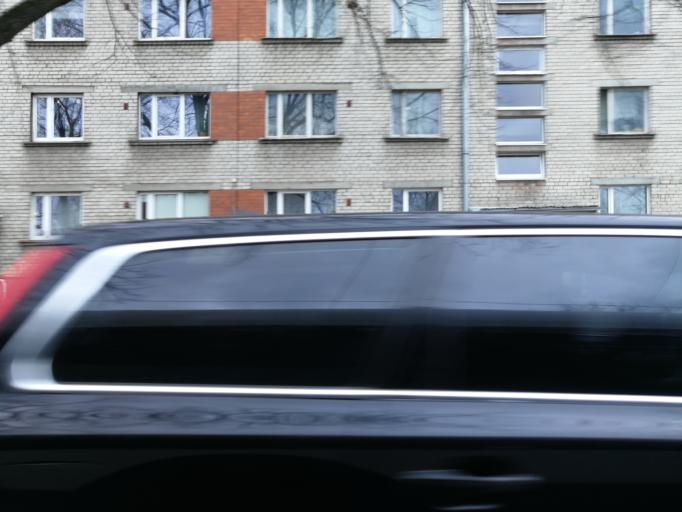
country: LV
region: Marupe
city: Marupe
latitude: 56.9383
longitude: 24.0418
